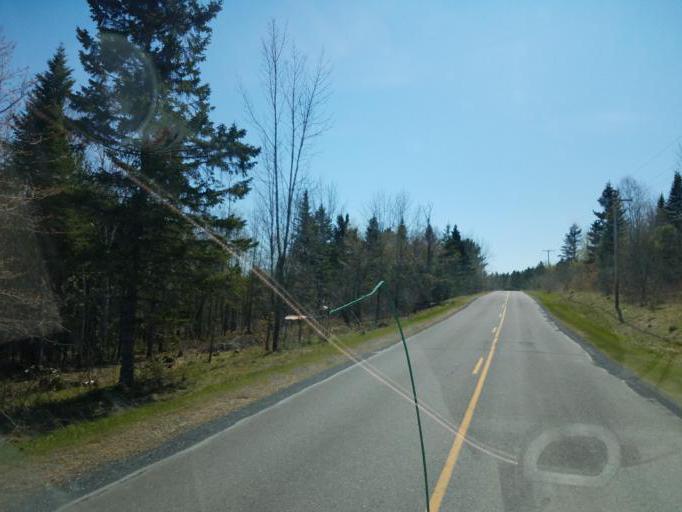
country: US
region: Maine
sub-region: Aroostook County
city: Caribou
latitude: 46.9484
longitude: -68.1054
